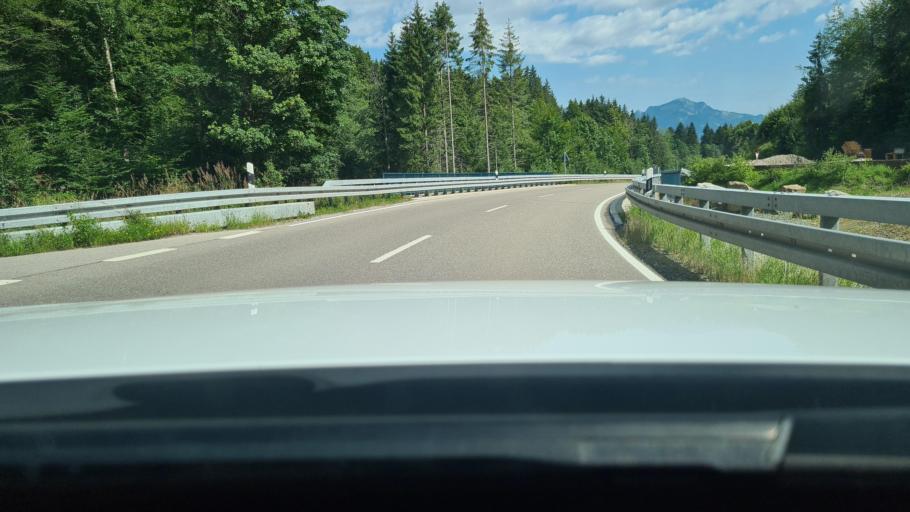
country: DE
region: Bavaria
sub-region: Swabia
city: Obermaiselstein
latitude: 47.4454
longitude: 10.2299
